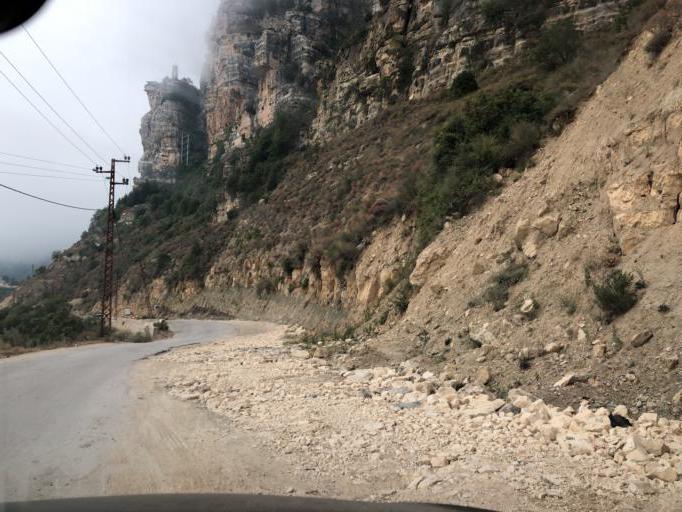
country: LB
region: Liban-Nord
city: Bcharre
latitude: 34.1119
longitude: 35.9078
